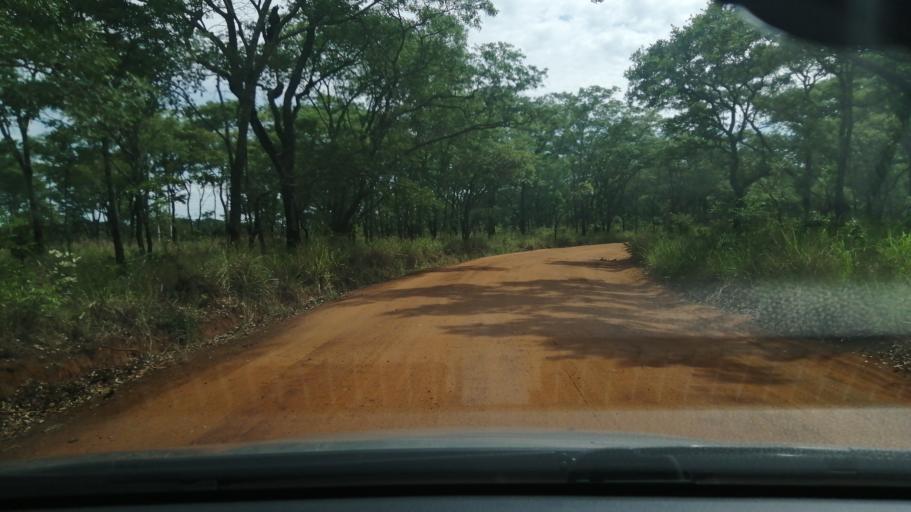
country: ZW
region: Mashonaland West
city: Norton
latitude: -17.8653
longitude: 30.8001
